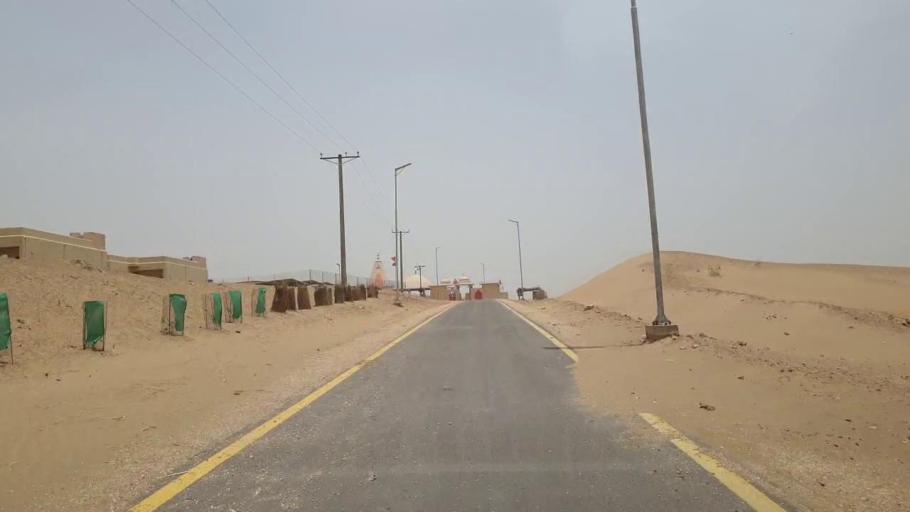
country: PK
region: Sindh
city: Islamkot
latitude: 24.7229
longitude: 70.3277
